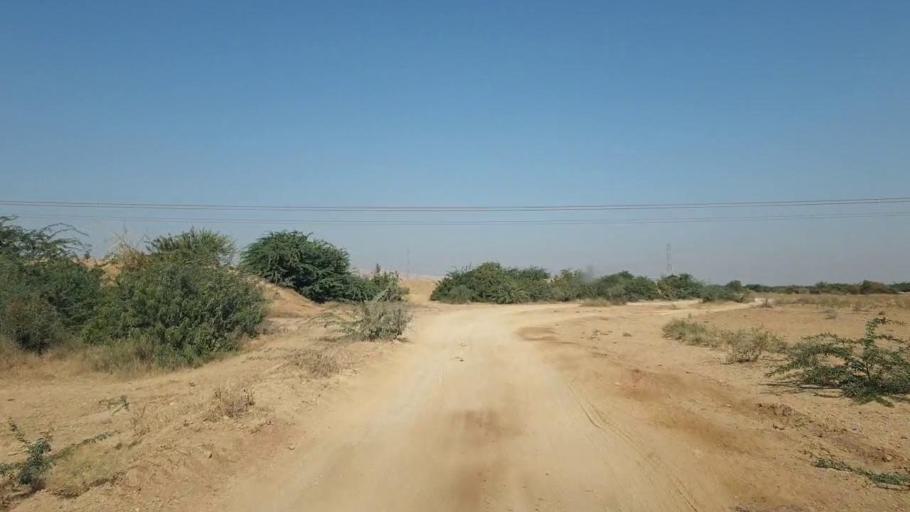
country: PK
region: Sindh
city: Gharo
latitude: 25.1880
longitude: 67.7380
